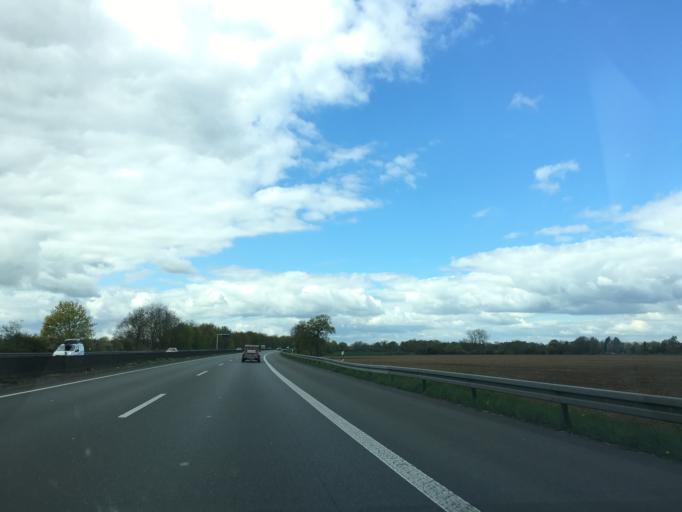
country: DE
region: North Rhine-Westphalia
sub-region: Regierungsbezirk Munster
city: Senden
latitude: 51.9003
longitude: 7.4794
